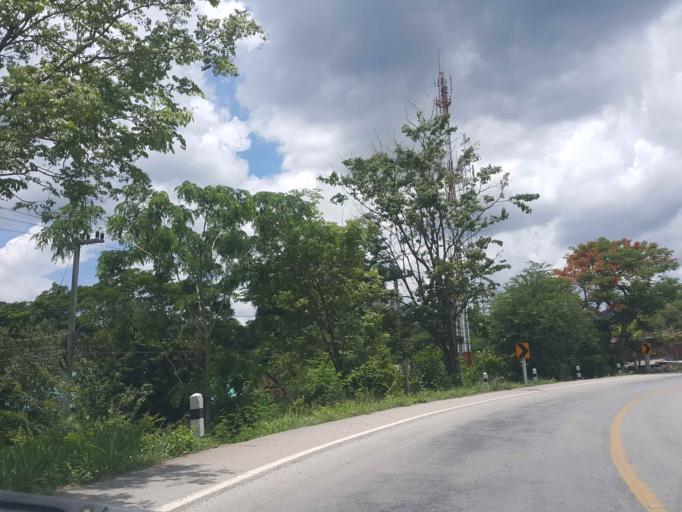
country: TH
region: Nan
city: Wiang Sa
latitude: 18.5211
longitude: 100.5591
